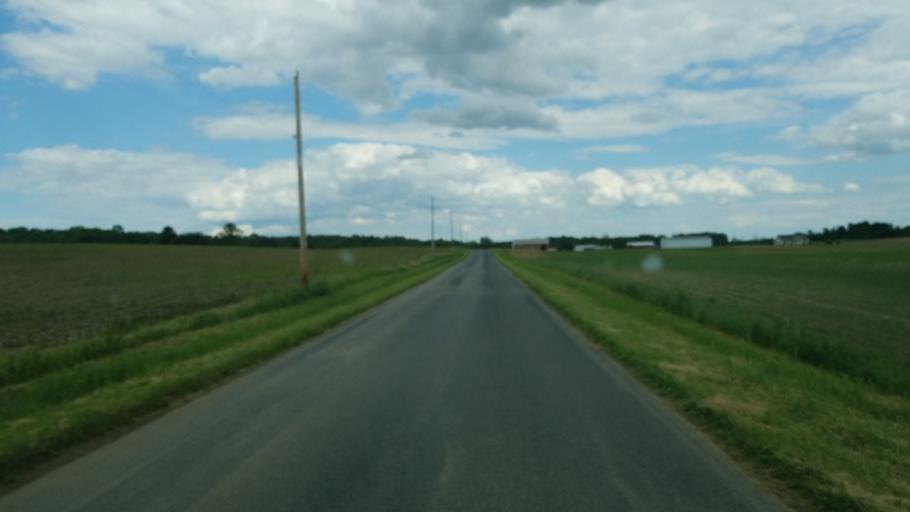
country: US
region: Ohio
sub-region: Richland County
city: Shelby
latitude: 40.9382
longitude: -82.5759
